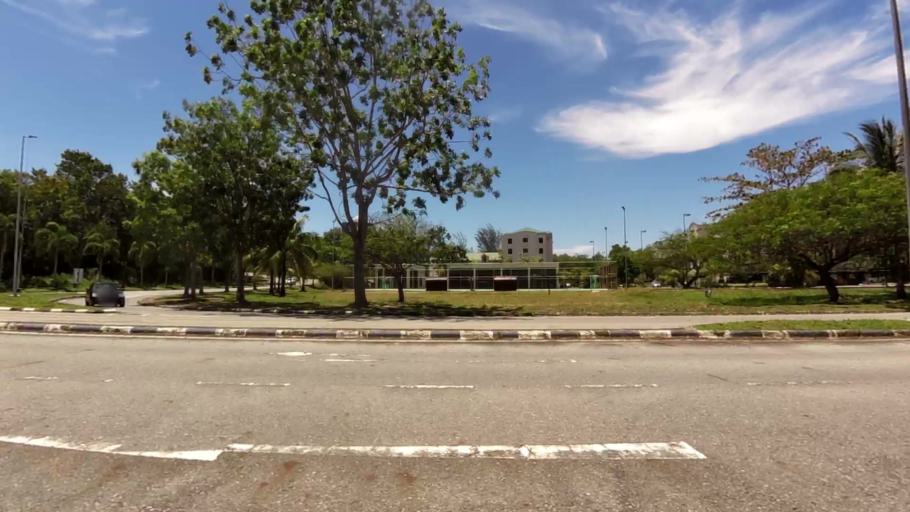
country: BN
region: Brunei and Muara
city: Bandar Seri Begawan
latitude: 4.9221
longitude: 114.9444
